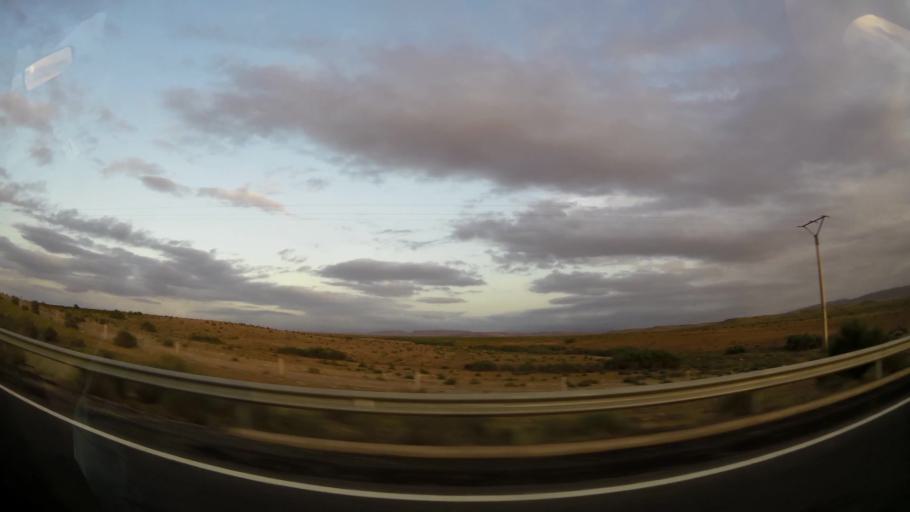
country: MA
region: Oriental
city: Taourirt
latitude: 34.5447
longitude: -2.9051
